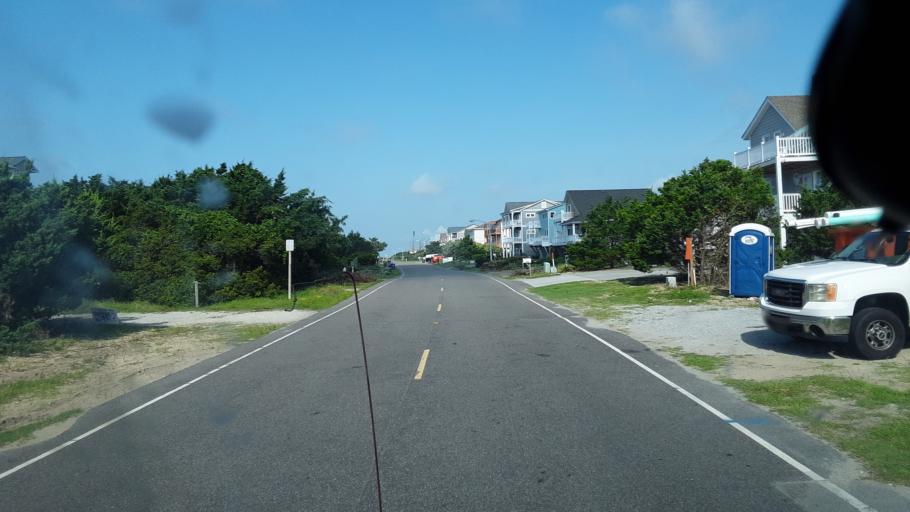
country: US
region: North Carolina
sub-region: Brunswick County
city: Southport
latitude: 33.8959
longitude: -78.0476
